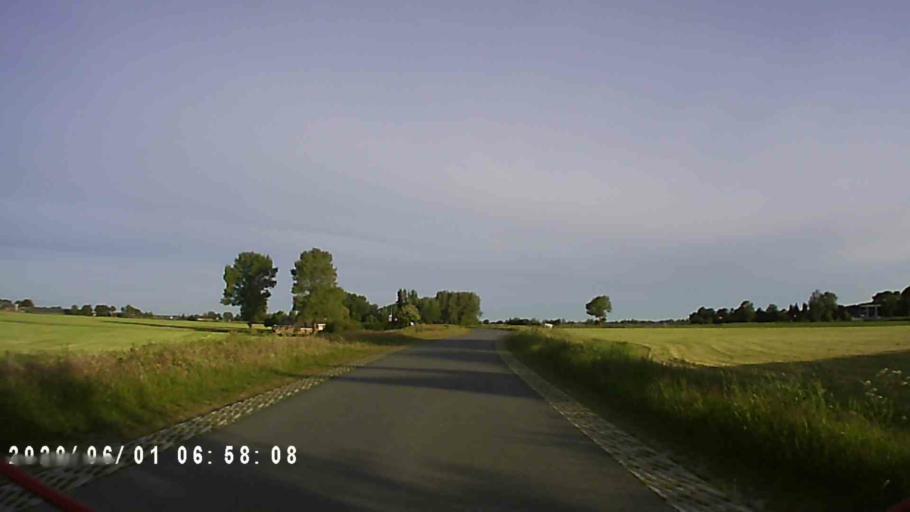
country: NL
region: Friesland
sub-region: Gemeente Dongeradeel
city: Anjum
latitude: 53.3192
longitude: 6.1026
